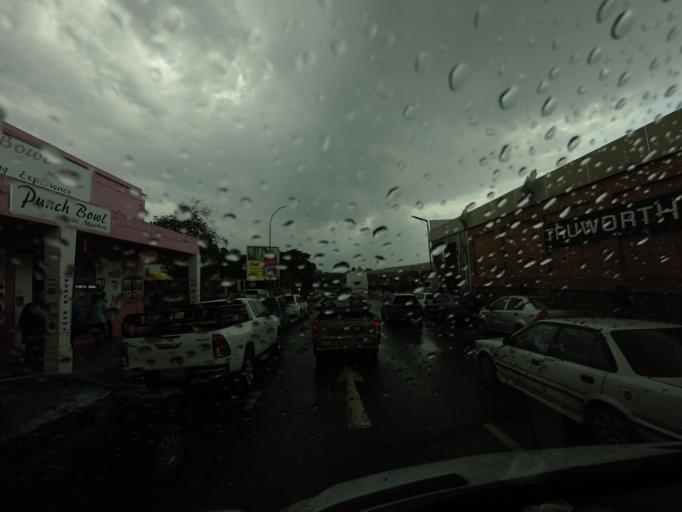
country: SZ
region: Manzini
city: Manzini
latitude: -26.4974
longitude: 31.3773
